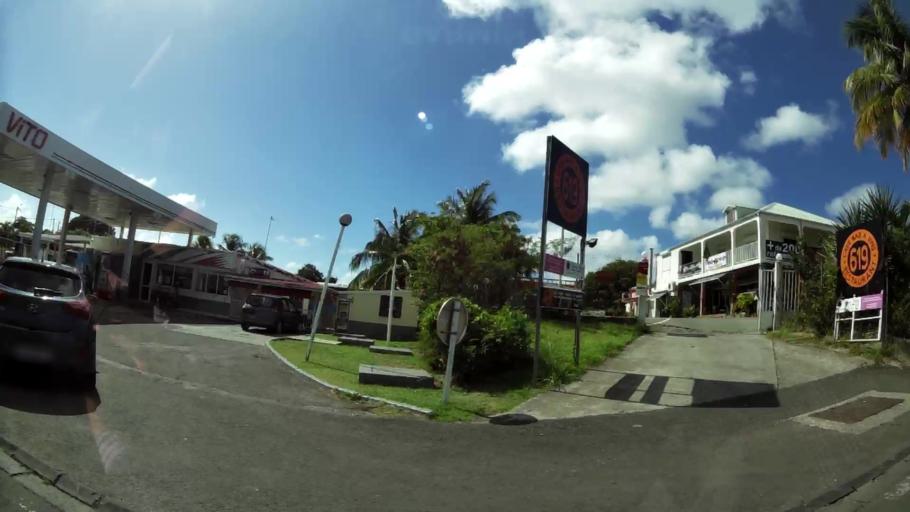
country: GP
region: Guadeloupe
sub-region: Guadeloupe
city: Saint-Francois
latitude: 16.2566
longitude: -61.2754
